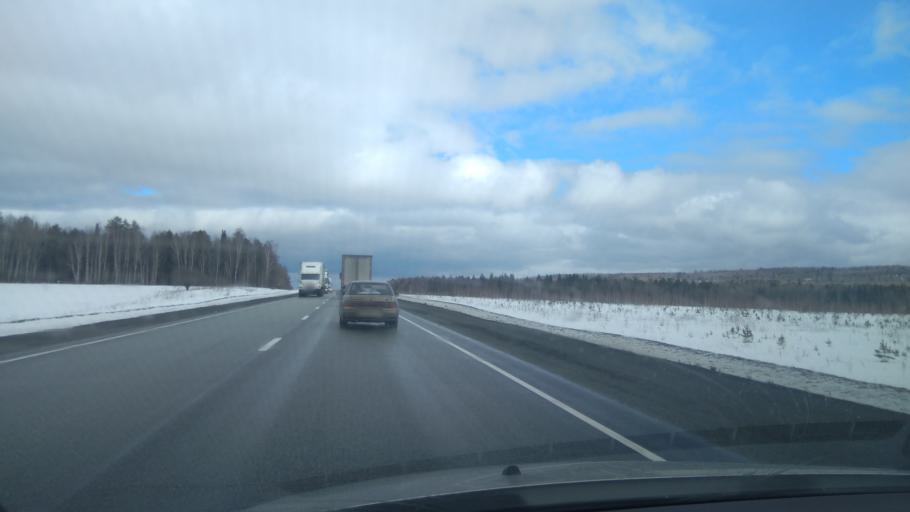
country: RU
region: Sverdlovsk
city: Bisert'
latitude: 56.8117
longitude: 58.7372
